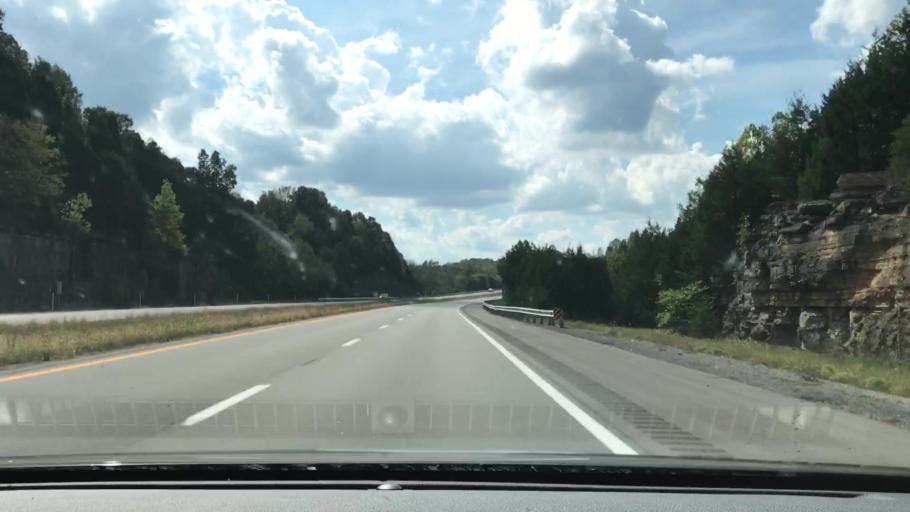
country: US
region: Kentucky
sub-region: Adair County
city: Columbia
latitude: 37.0466
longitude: -85.4464
